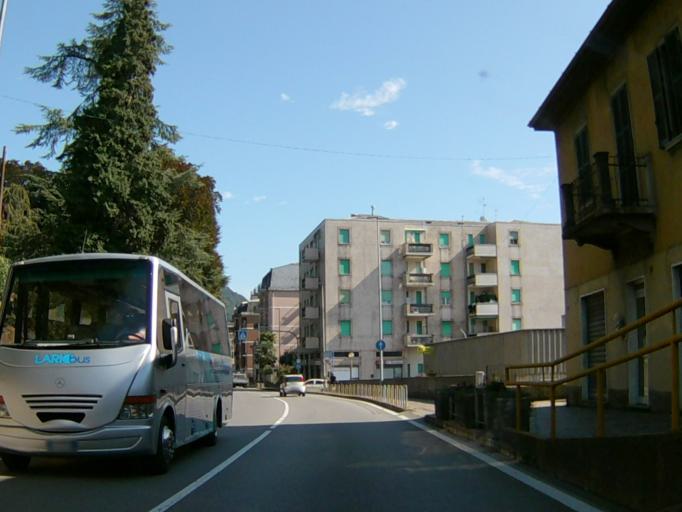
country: IT
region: Lombardy
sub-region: Provincia di Lecco
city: Vercurago
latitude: 45.8039
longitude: 9.4270
